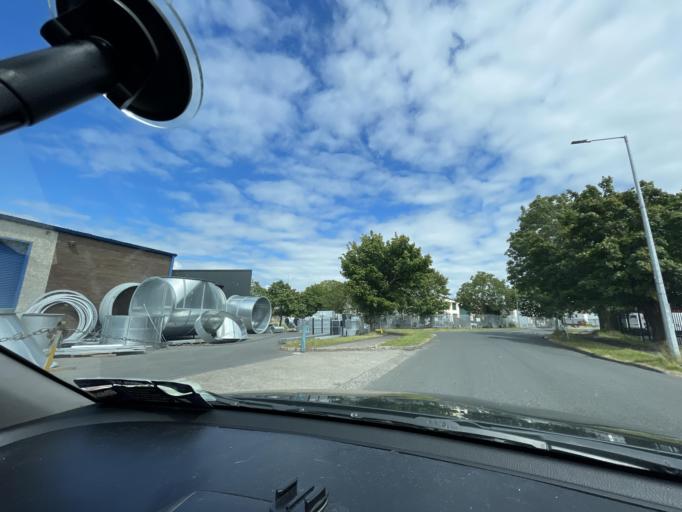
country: IE
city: Cherry Orchard
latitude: 53.3220
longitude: -6.3648
